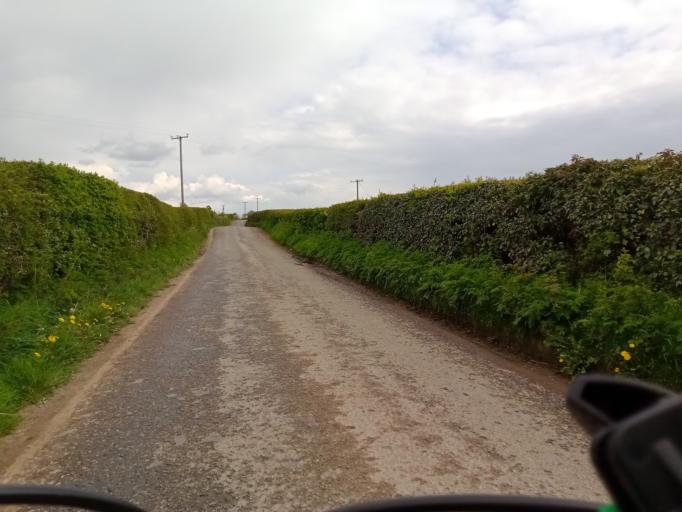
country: IE
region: Leinster
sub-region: Kilkenny
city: Kilkenny
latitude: 52.6002
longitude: -7.2568
